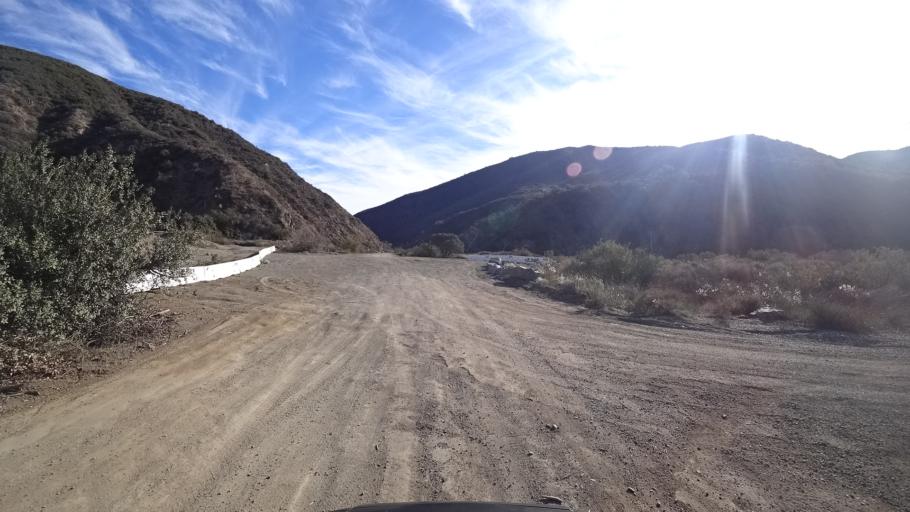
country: US
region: California
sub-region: Orange County
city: Trabuco Canyon
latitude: 33.6717
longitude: -117.5593
